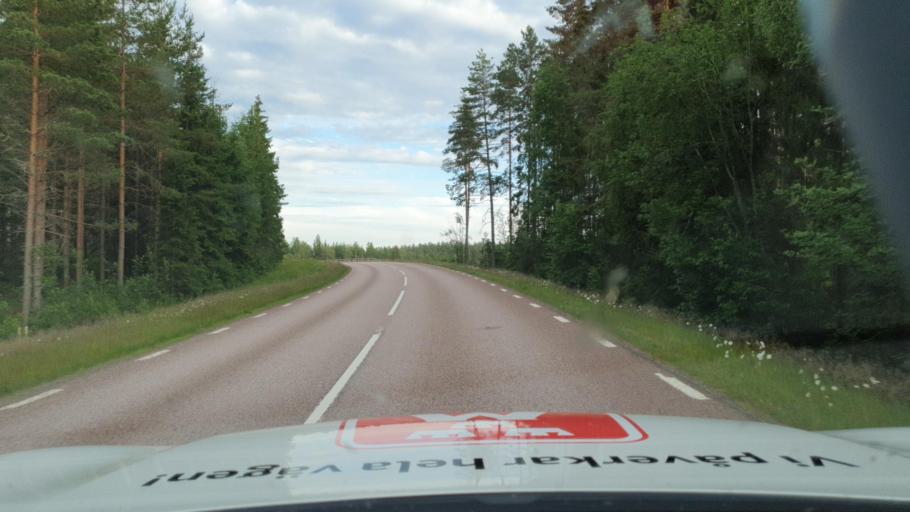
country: SE
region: Vaermland
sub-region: Karlstads Kommun
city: Molkom
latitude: 59.5403
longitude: 13.7768
